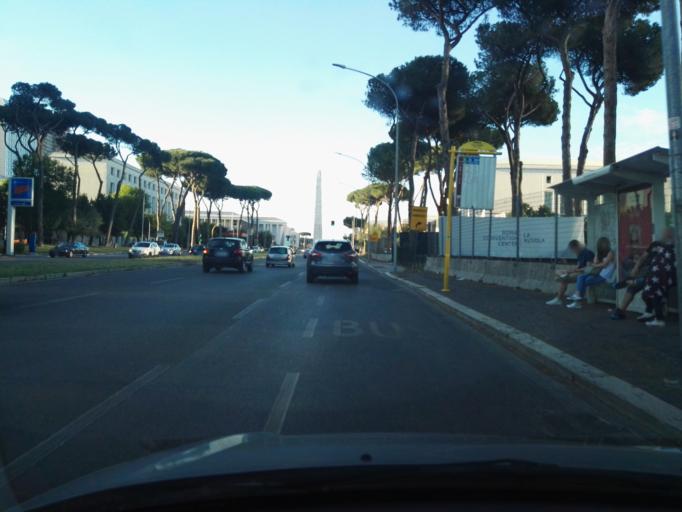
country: IT
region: Latium
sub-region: Citta metropolitana di Roma Capitale
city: Selcetta
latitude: 41.8310
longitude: 12.4696
